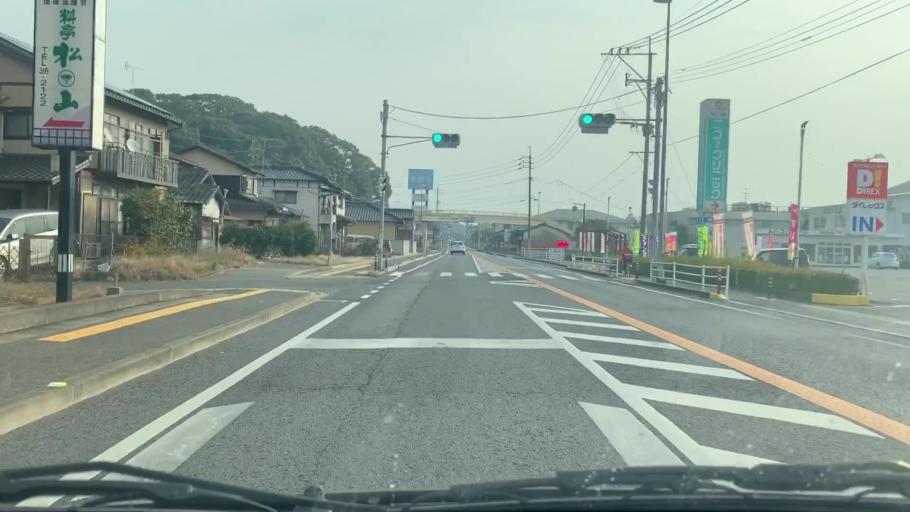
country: JP
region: Saga Prefecture
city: Takeocho-takeo
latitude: 33.2203
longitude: 130.0669
